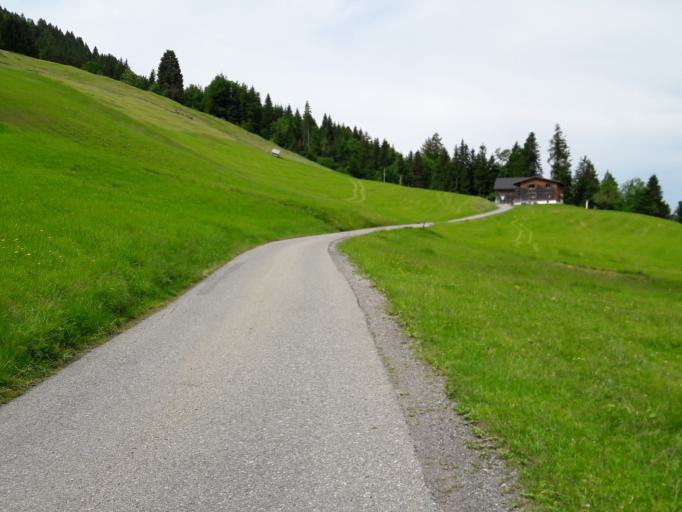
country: AT
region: Vorarlberg
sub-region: Politischer Bezirk Bludenz
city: Raggal
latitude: 47.2086
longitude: 9.8240
